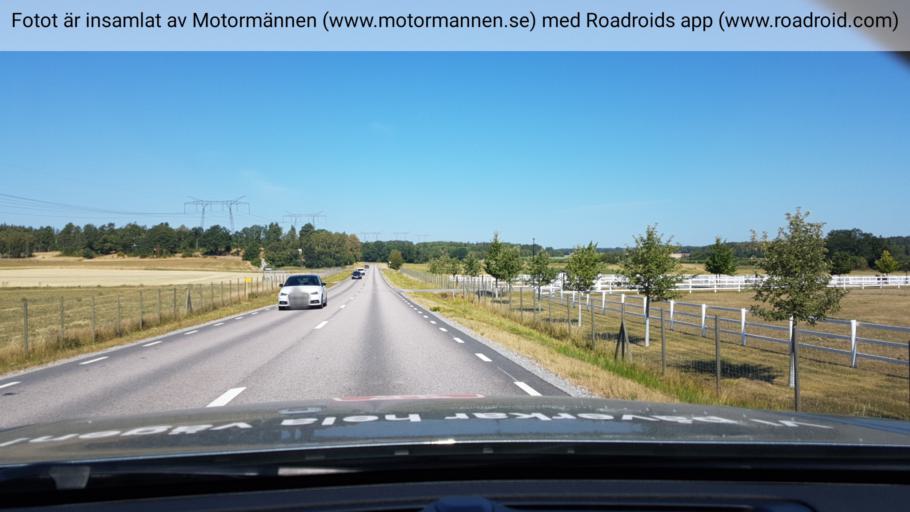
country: SE
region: Stockholm
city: Stenhamra
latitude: 59.3433
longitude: 17.6345
